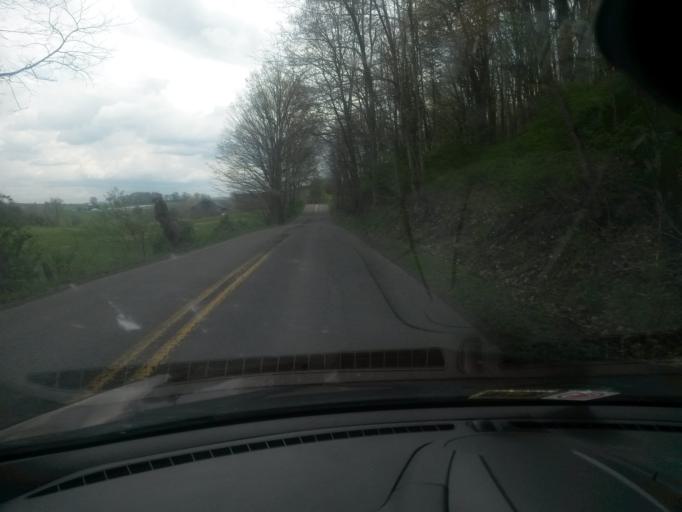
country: US
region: West Virginia
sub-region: Greenbrier County
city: Lewisburg
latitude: 37.8926
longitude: -80.4316
